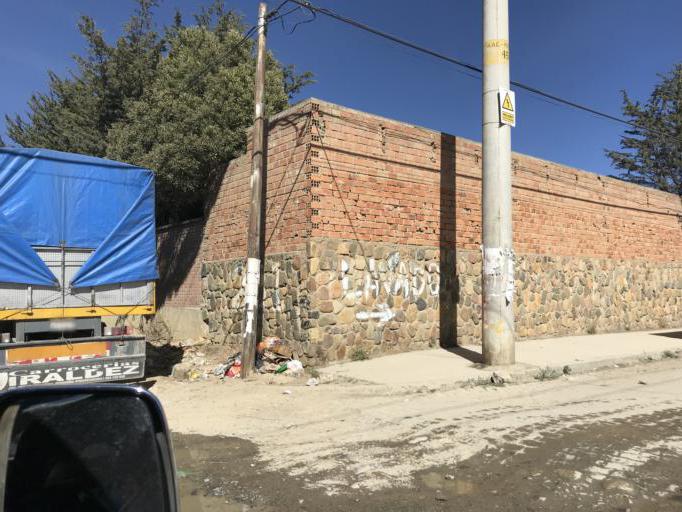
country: BO
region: La Paz
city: La Paz
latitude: -16.4871
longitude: -68.2109
